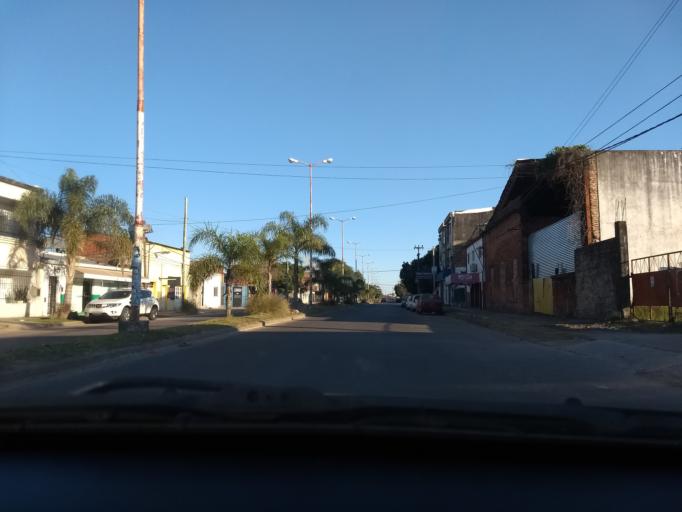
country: AR
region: Corrientes
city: Corrientes
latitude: -27.4735
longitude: -58.8134
